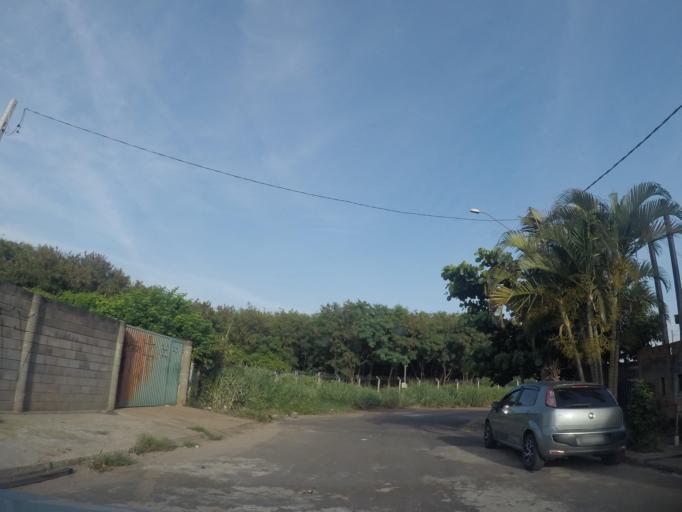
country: BR
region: Sao Paulo
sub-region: Hortolandia
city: Hortolandia
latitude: -22.8244
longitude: -47.1915
